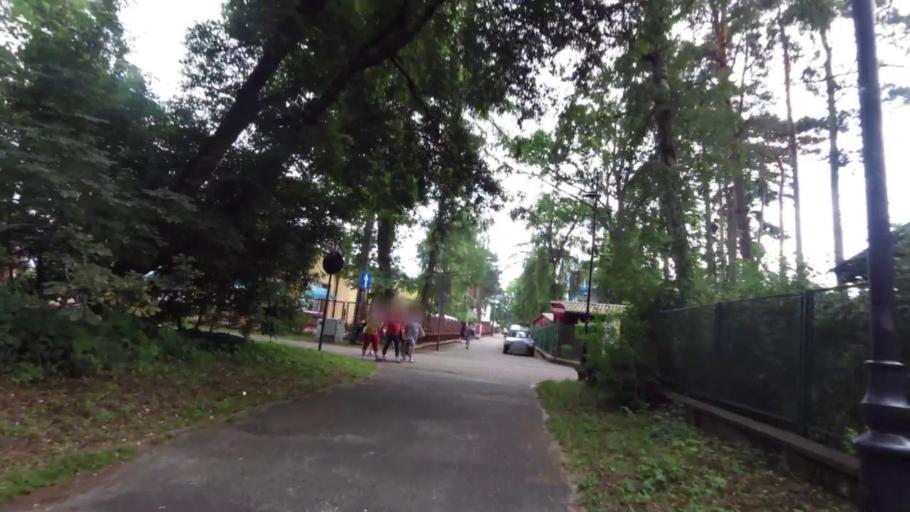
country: PL
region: West Pomeranian Voivodeship
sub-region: Powiat gryficki
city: Mrzezyno
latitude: 54.1464
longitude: 15.2989
